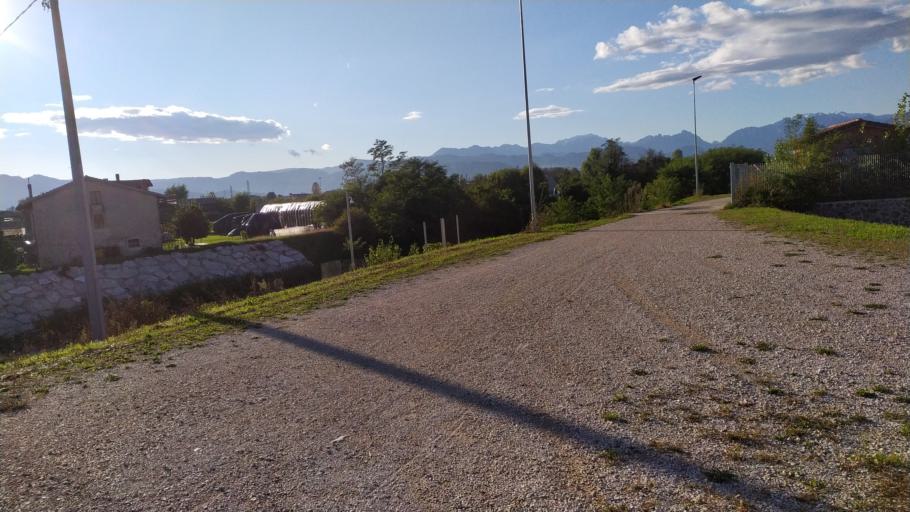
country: IT
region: Veneto
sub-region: Provincia di Vicenza
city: Novoledo
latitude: 45.6327
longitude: 11.4997
